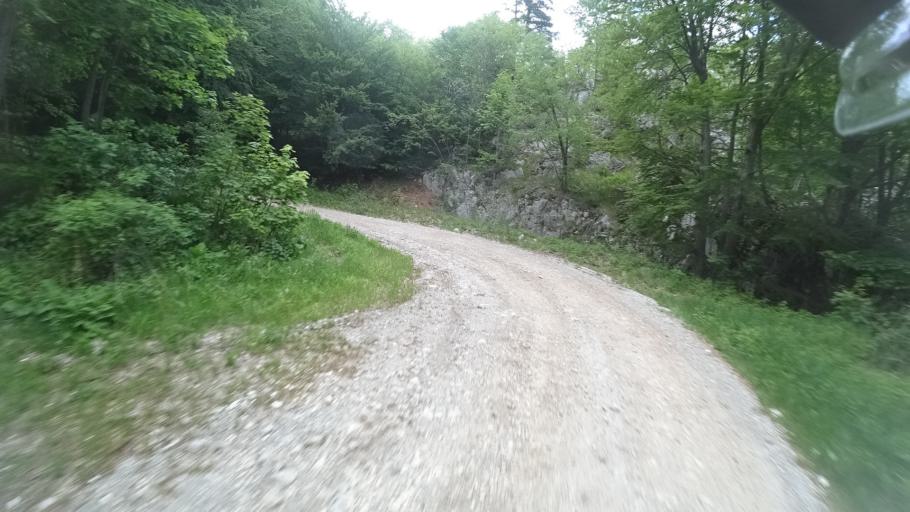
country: HR
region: Licko-Senjska
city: Gospic
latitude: 44.4683
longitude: 15.2964
